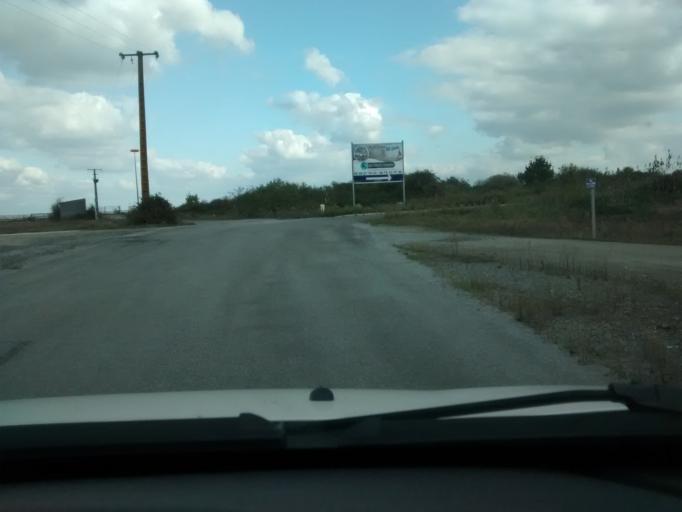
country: FR
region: Pays de la Loire
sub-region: Departement de la Loire-Atlantique
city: Saint-Paimboeuf
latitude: 47.2845
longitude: -2.0014
